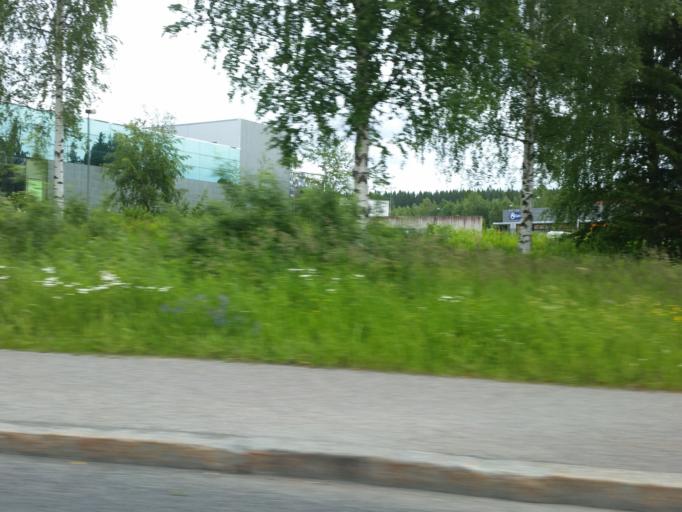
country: FI
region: Northern Savo
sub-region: Kuopio
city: Kuopio
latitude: 62.8856
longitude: 27.6293
